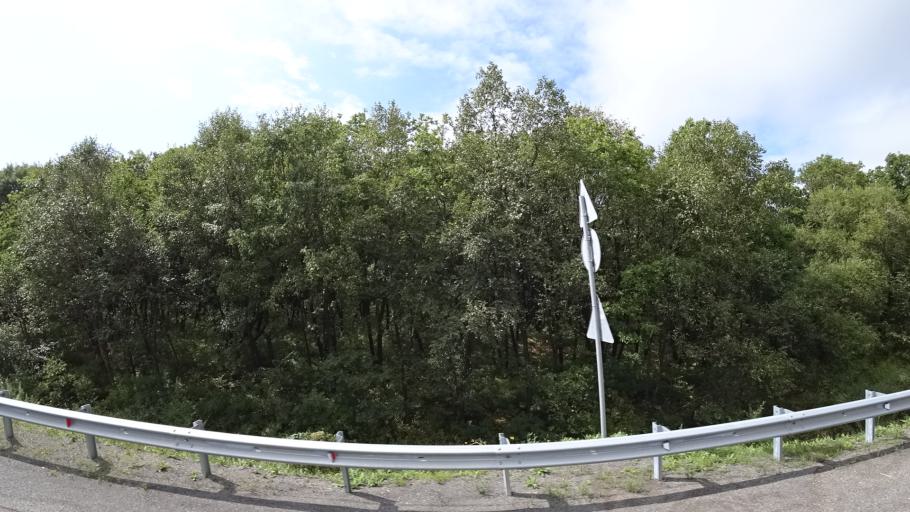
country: RU
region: Primorskiy
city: Lyalichi
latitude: 44.1366
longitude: 132.4281
